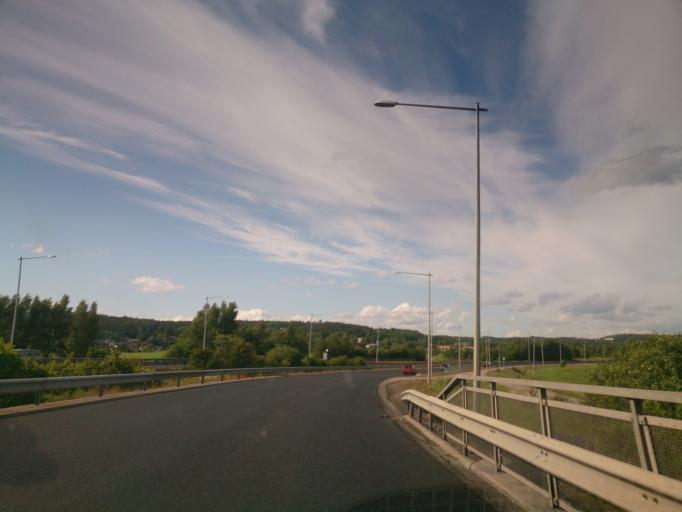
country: SE
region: OEstergoetland
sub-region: Norrkopings Kommun
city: Jursla
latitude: 58.6445
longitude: 16.1637
